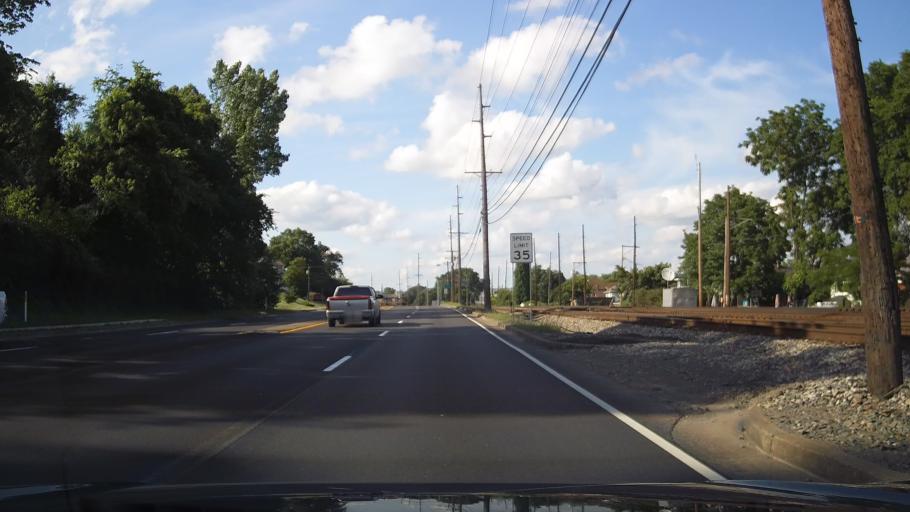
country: US
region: Kentucky
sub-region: Boyd County
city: Catlettsburg
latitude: 38.4099
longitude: -82.5995
